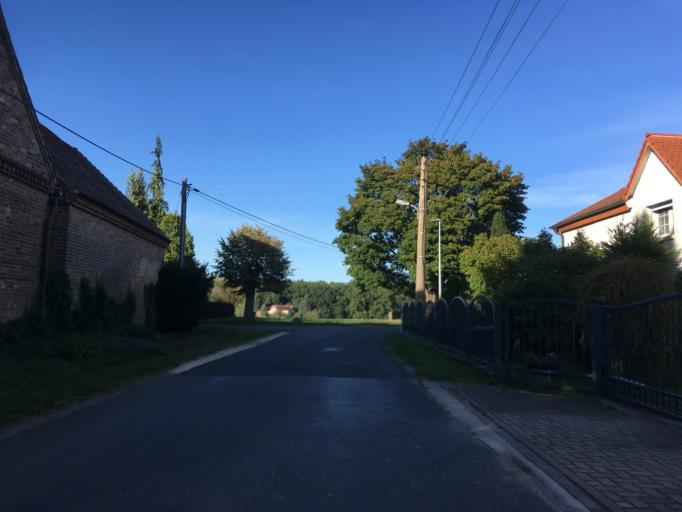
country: DE
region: Saxony
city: Bad Muskau
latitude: 51.5793
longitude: 14.7230
